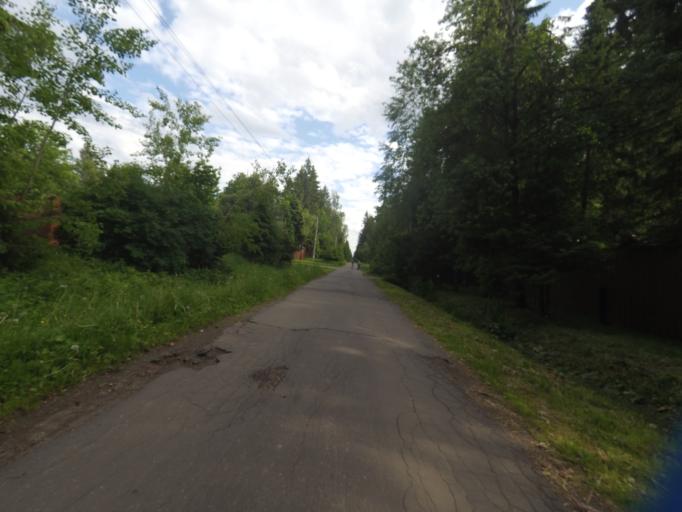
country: RU
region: Moskovskaya
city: Nekrasovskiy
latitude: 56.1176
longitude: 37.5173
